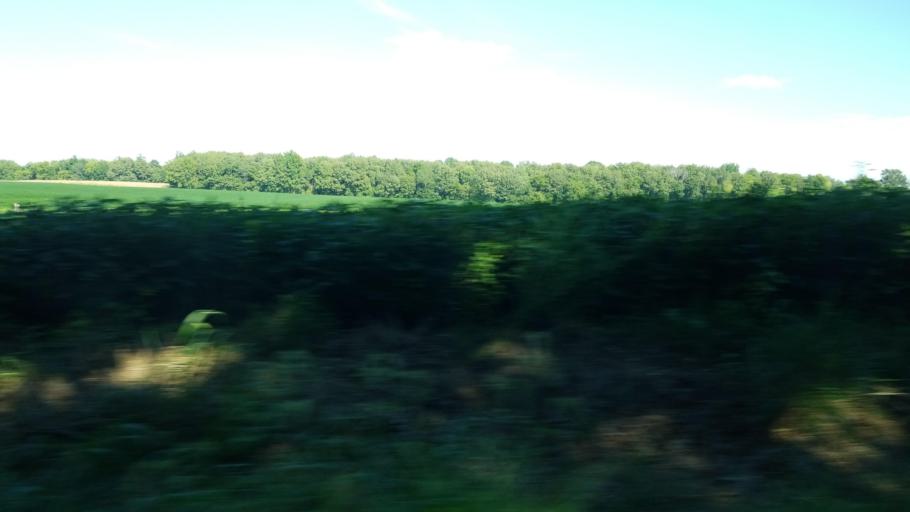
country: US
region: Illinois
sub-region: Saline County
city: Harrisburg
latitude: 37.8187
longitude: -88.5672
